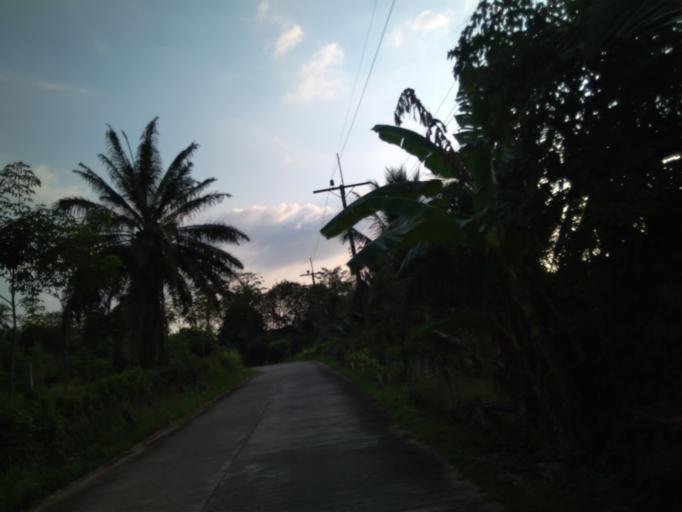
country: TH
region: Phangnga
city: Ko Yao
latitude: 8.1396
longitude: 98.5984
